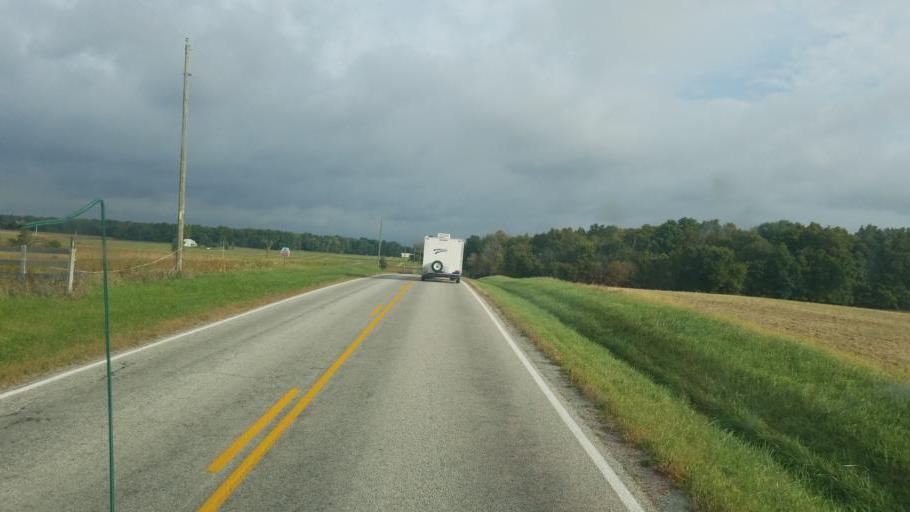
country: US
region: Ohio
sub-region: Seneca County
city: Fostoria
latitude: 41.0466
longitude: -83.4772
